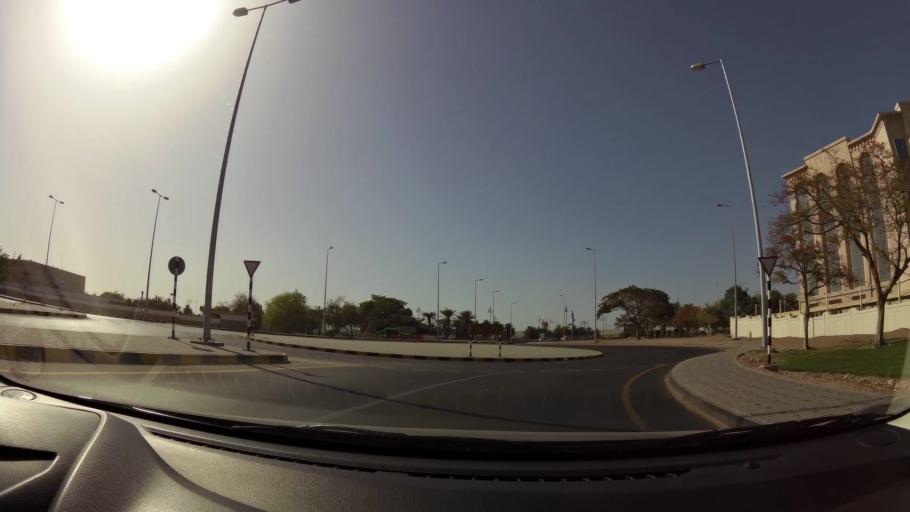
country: OM
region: Muhafazat Masqat
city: Bawshar
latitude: 23.5845
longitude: 58.2910
